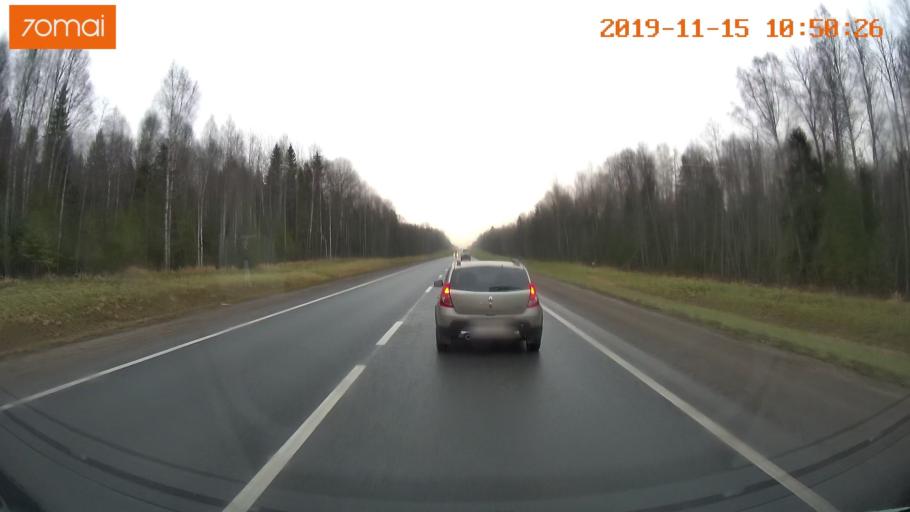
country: RU
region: Vologda
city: Chebsara
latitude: 59.1853
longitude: 38.6814
